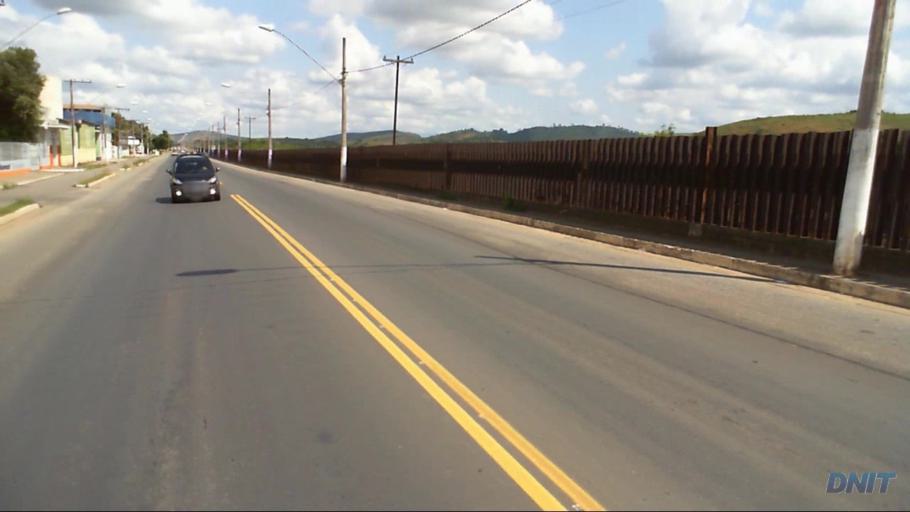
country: BR
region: Minas Gerais
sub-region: Governador Valadares
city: Governador Valadares
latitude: -18.8930
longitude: -41.9782
